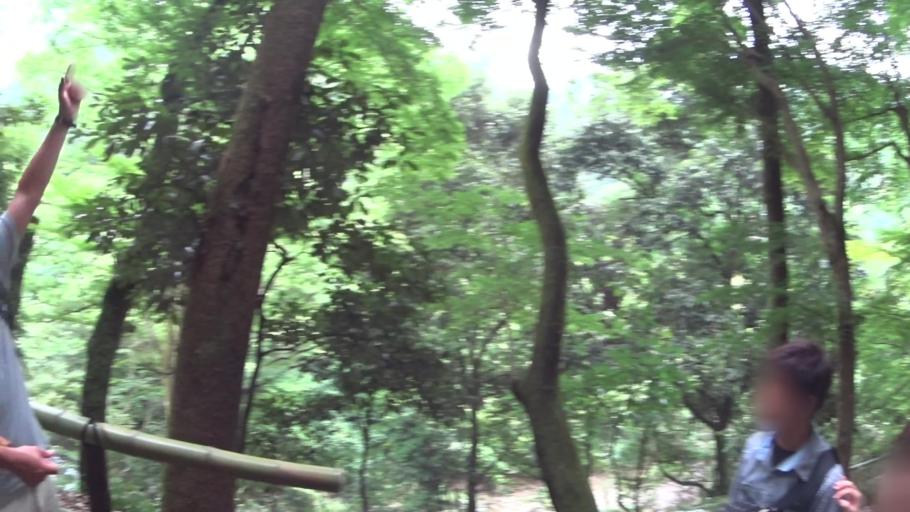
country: JP
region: Kyoto
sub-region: Kyoto-shi
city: Kamigyo-ku
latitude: 35.0594
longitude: 135.6778
